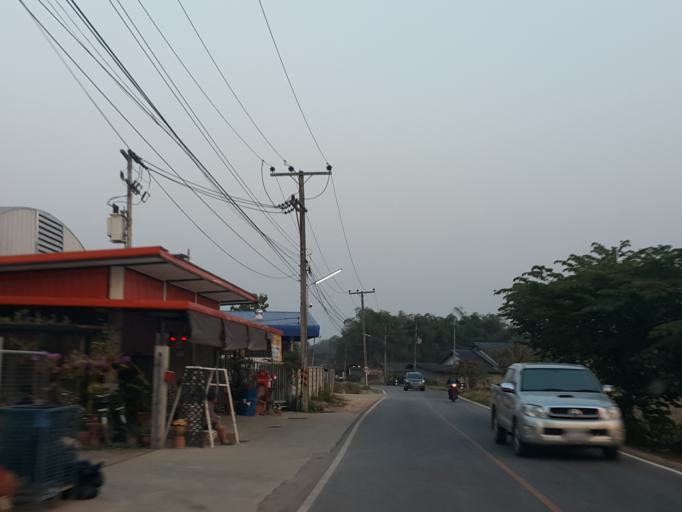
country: TH
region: Chiang Mai
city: Mae Taeng
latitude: 19.0173
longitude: 98.8780
